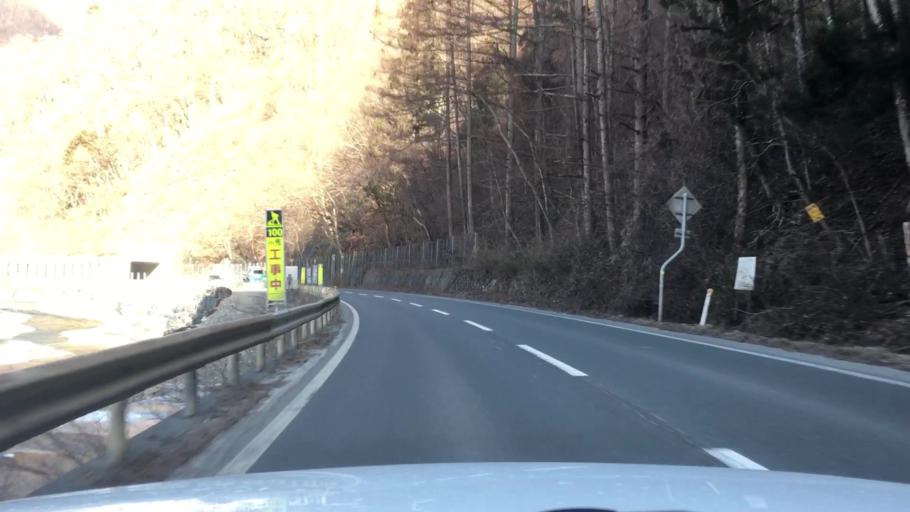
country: JP
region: Iwate
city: Miyako
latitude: 39.6032
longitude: 141.6522
